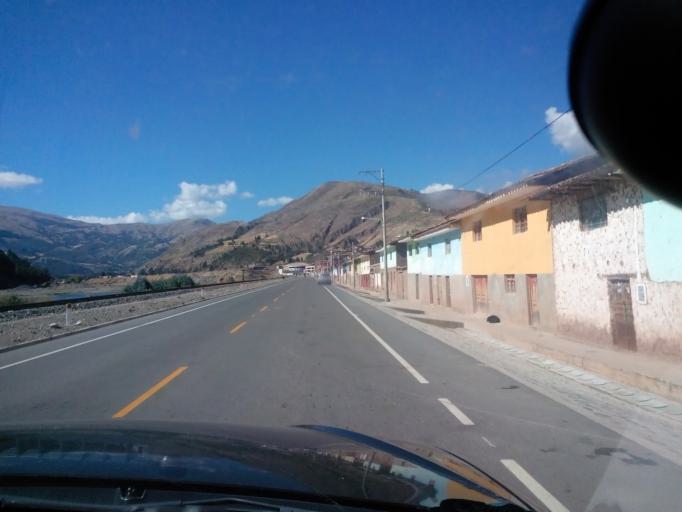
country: PE
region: Cusco
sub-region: Provincia de Quispicanchis
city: Urcos
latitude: -13.6779
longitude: -71.6283
